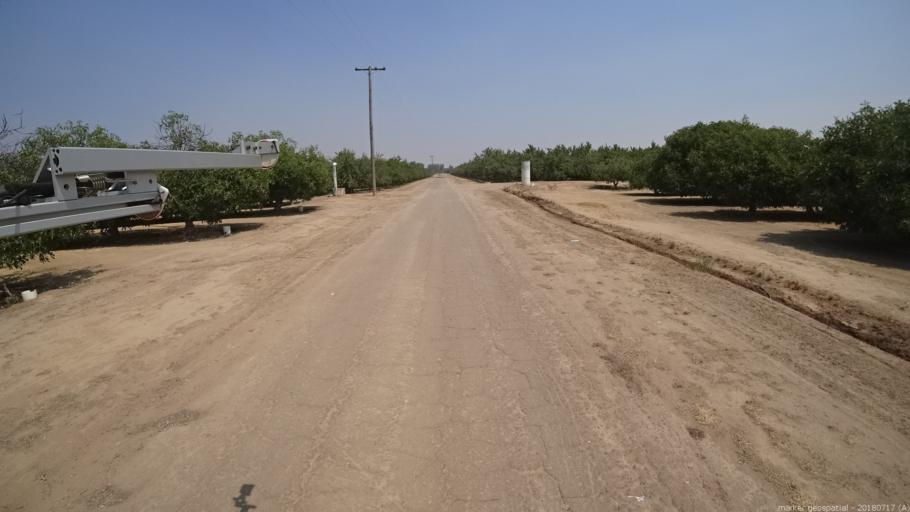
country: US
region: California
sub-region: Madera County
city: Fairmead
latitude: 37.1375
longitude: -120.1471
